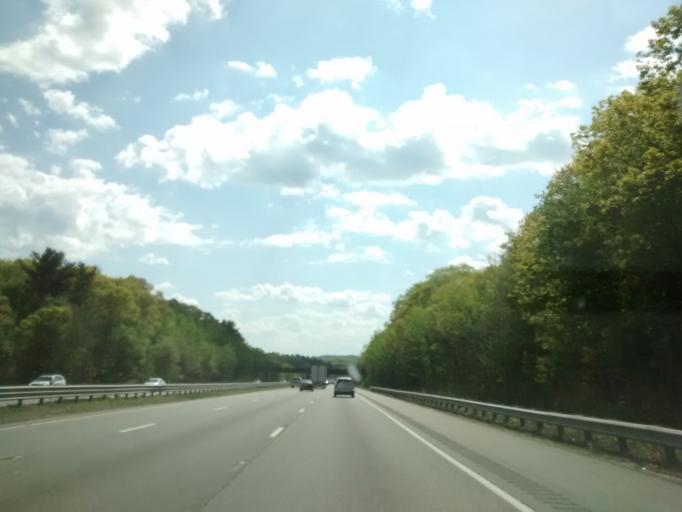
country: US
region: Massachusetts
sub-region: Worcester County
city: Charlton
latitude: 42.1694
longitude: -71.9344
